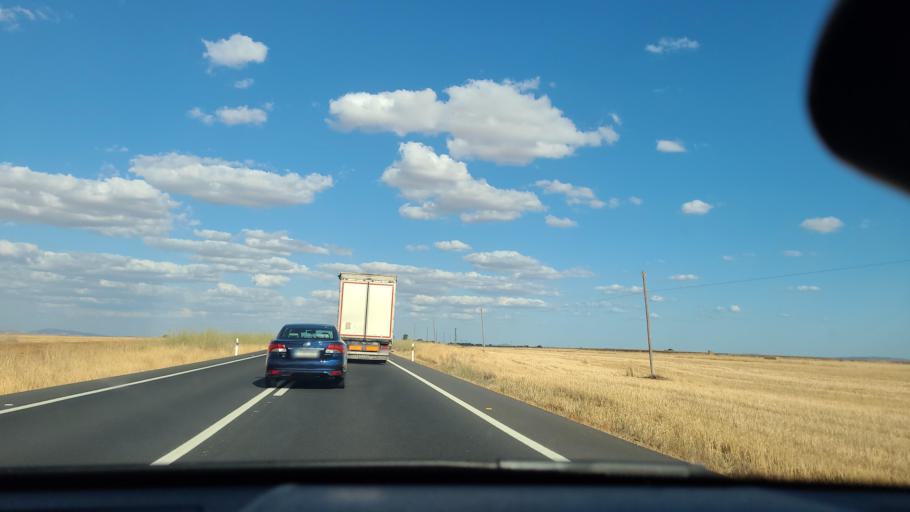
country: ES
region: Extremadura
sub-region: Provincia de Badajoz
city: Azuaga
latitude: 38.2645
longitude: -5.7424
